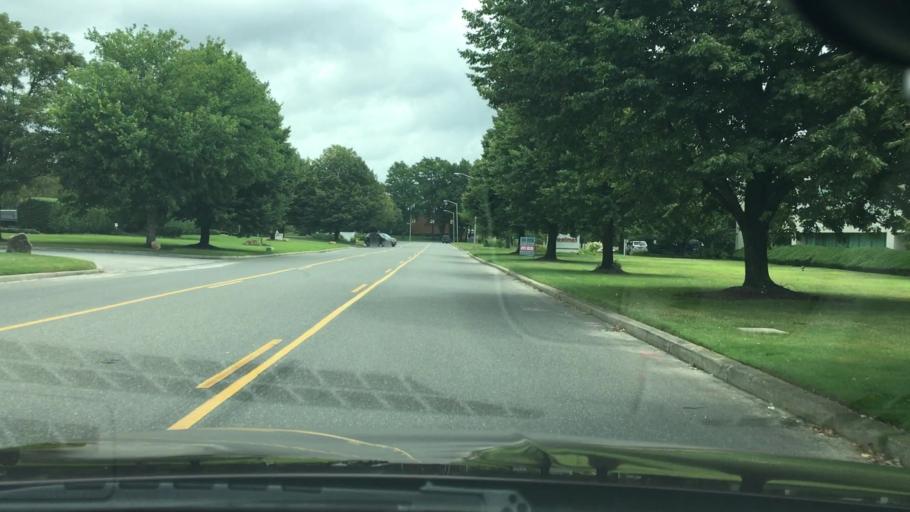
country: US
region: New York
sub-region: Suffolk County
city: Brentwood
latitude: 40.8136
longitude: -73.2586
